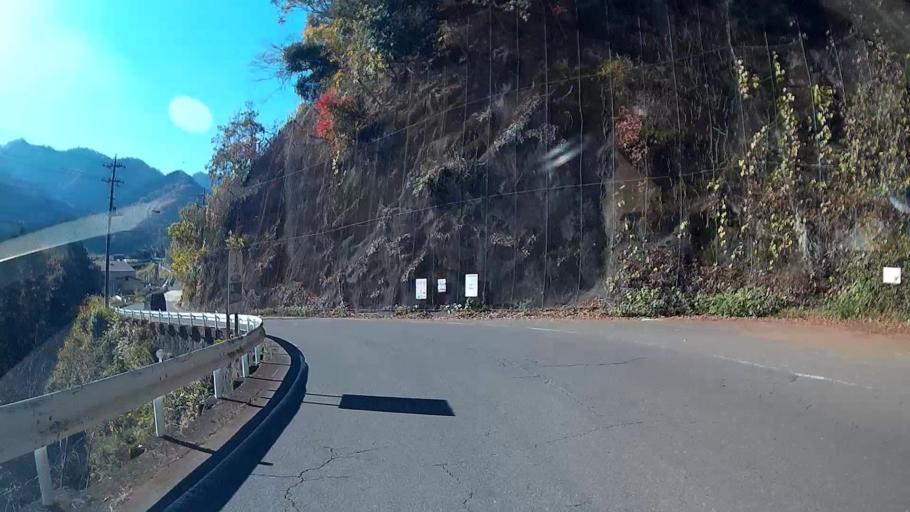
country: JP
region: Yamanashi
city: Uenohara
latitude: 35.5778
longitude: 139.0973
